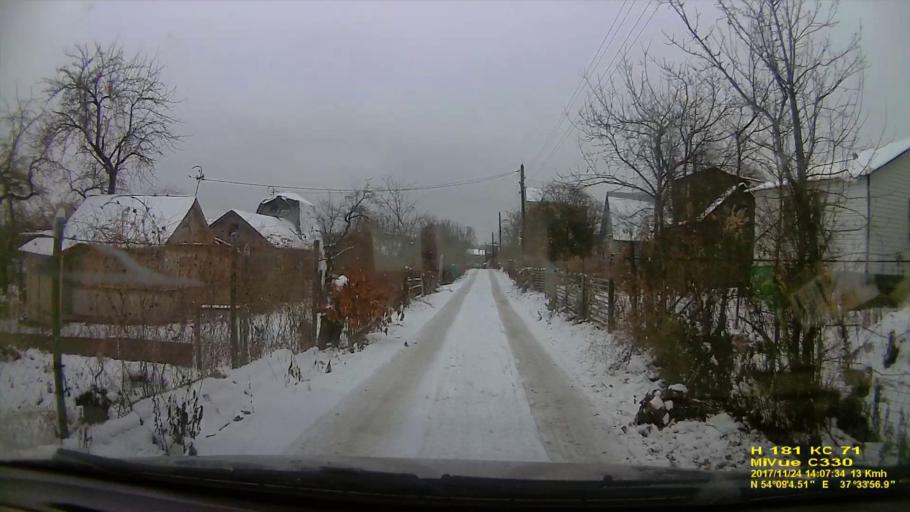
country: RU
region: Tula
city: Mendeleyevskiy
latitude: 54.1509
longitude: 37.5645
